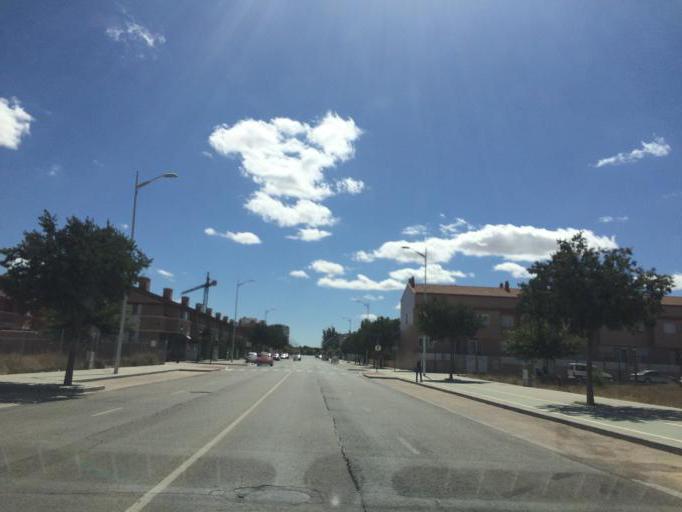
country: ES
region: Castille-La Mancha
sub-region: Provincia de Albacete
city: Albacete
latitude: 38.9824
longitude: -1.8420
